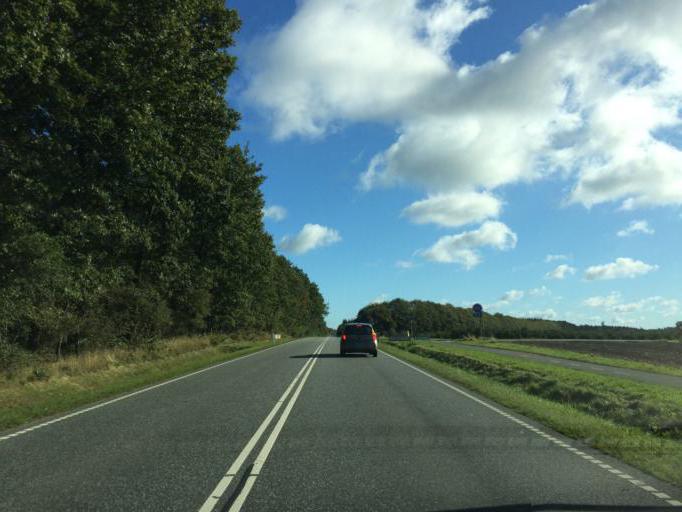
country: DK
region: Central Jutland
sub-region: Holstebro Kommune
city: Vinderup
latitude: 56.3922
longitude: 8.8229
